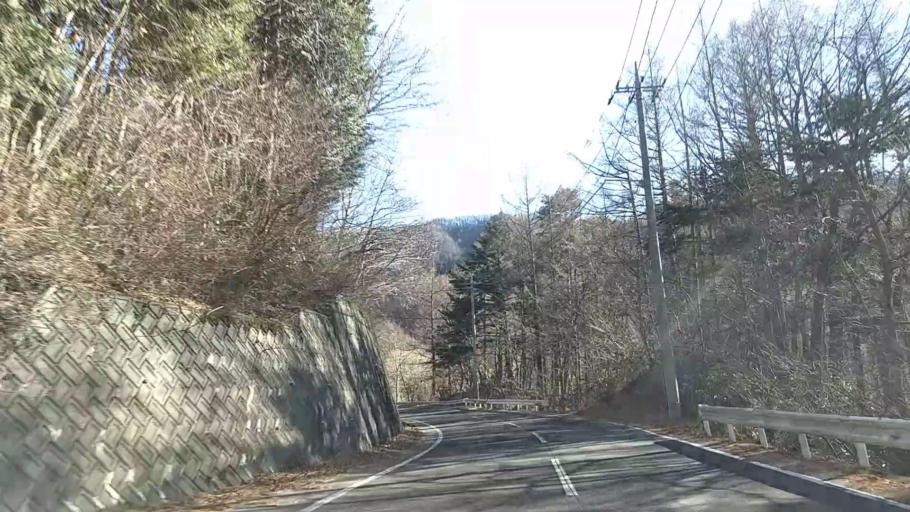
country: JP
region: Yamanashi
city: Otsuki
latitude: 35.5125
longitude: 138.9639
